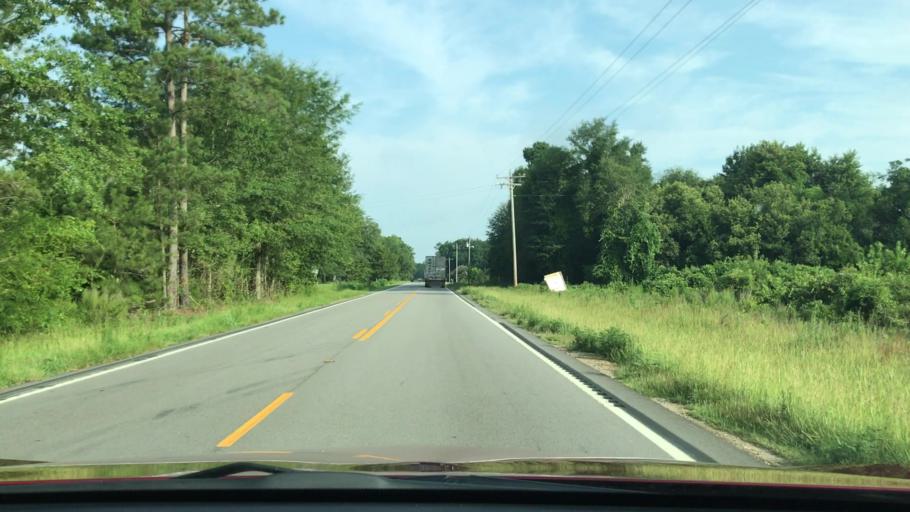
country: US
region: South Carolina
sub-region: Barnwell County
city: Blackville
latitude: 33.5542
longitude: -81.1621
